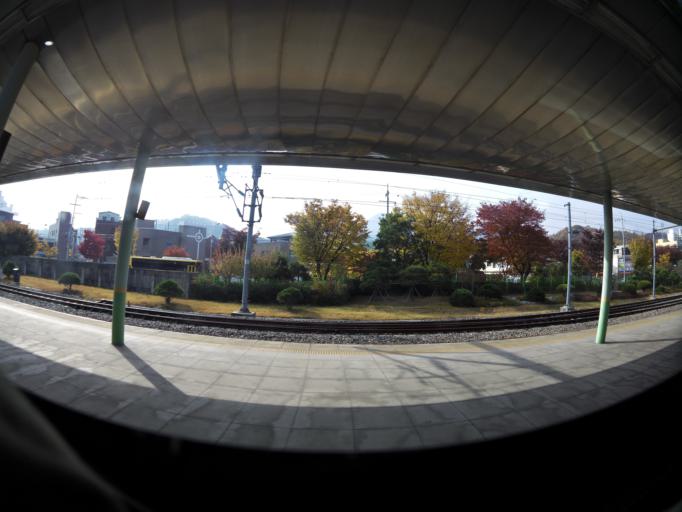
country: KR
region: Gyeongsangbuk-do
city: Gumi
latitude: 36.1272
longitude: 128.3335
